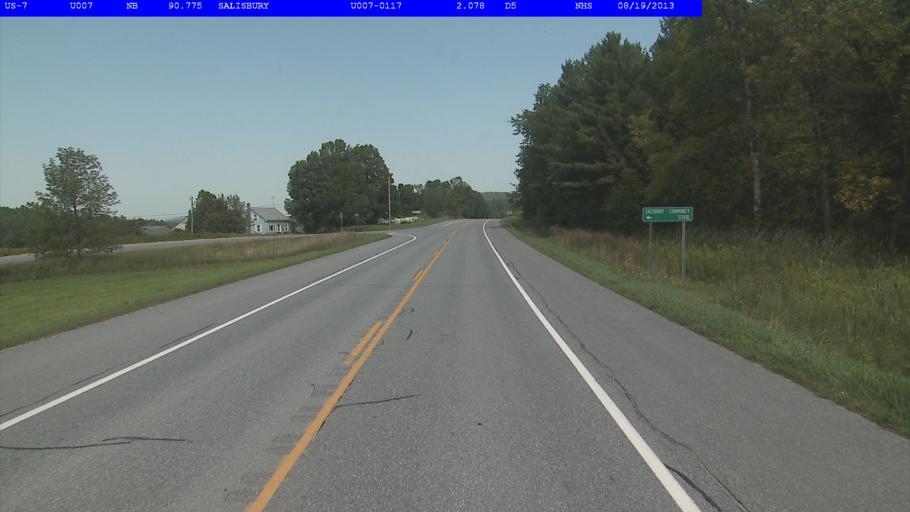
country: US
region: Vermont
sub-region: Addison County
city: Middlebury (village)
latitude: 43.9218
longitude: -73.1113
